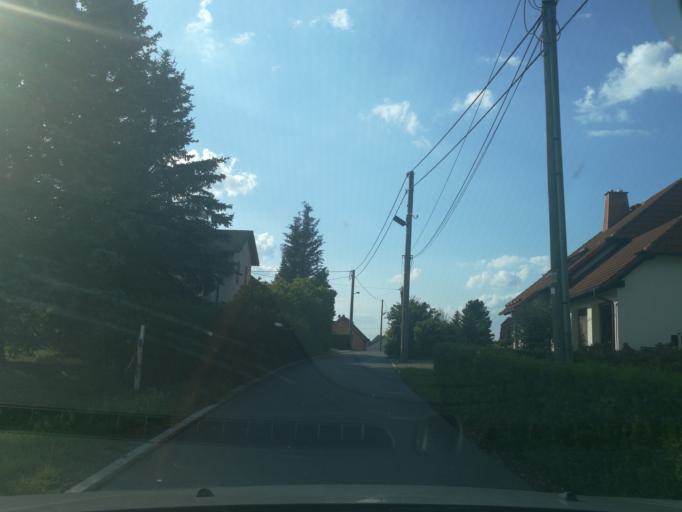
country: DE
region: Saxony
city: Adorf
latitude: 50.3053
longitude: 12.2768
